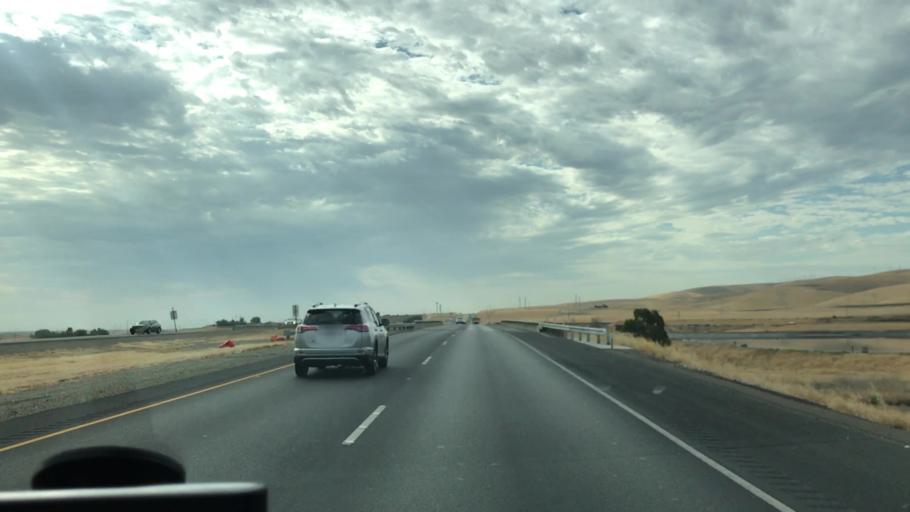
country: US
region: California
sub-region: San Joaquin County
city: Mountain House
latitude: 37.7136
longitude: -121.5260
